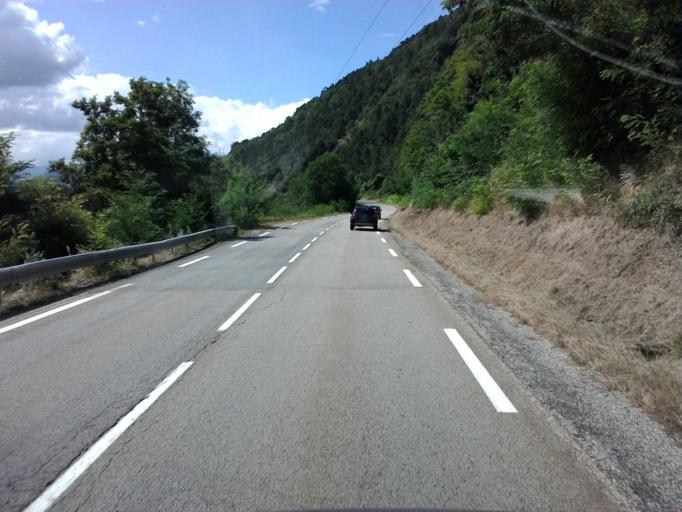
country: FR
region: Rhone-Alpes
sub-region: Departement de l'Isere
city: La Mure
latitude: 44.8424
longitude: 5.8712
